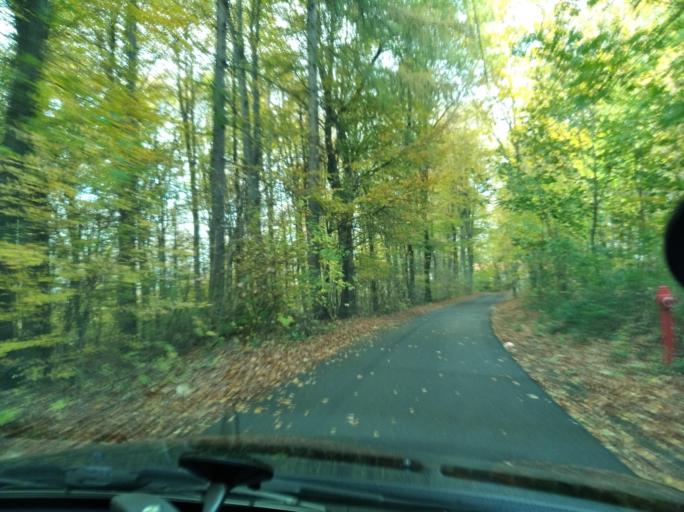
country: PL
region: Subcarpathian Voivodeship
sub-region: Powiat debicki
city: Debica
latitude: 50.0323
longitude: 21.4540
